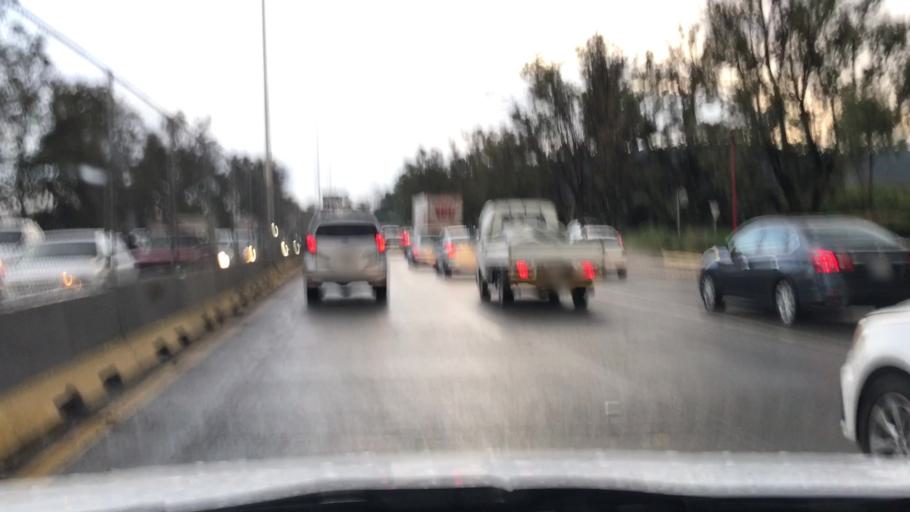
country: MX
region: Jalisco
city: Guadalajara
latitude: 20.6776
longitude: -103.4552
